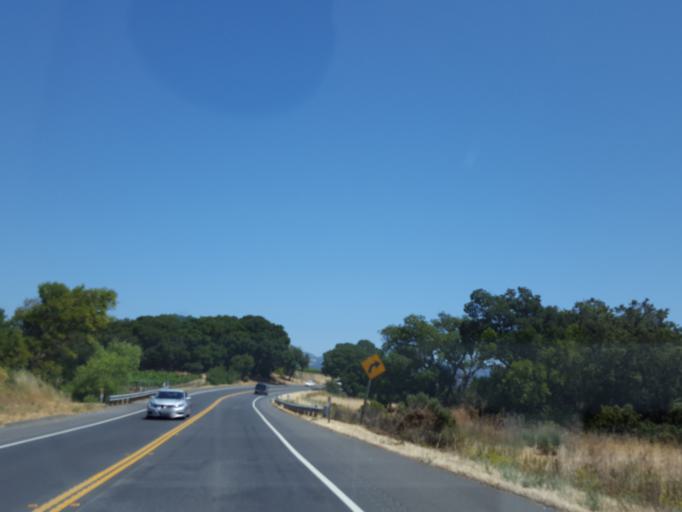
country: US
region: California
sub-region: Sonoma County
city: Temelec
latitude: 38.2463
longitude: -122.5011
